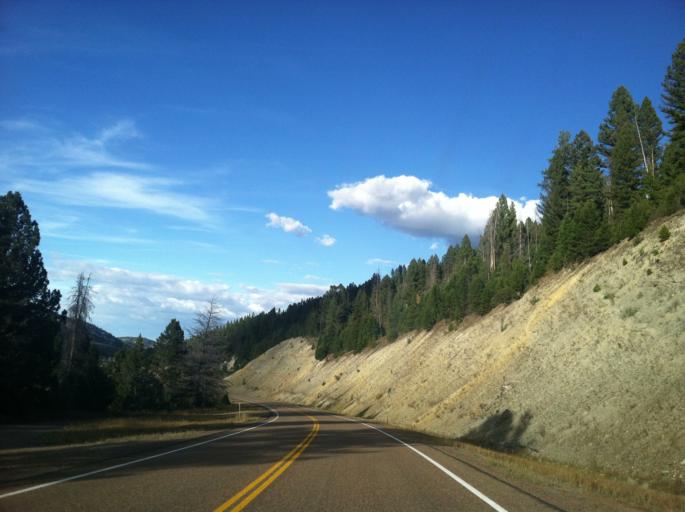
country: US
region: Montana
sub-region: Granite County
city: Philipsburg
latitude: 46.4008
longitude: -113.2987
